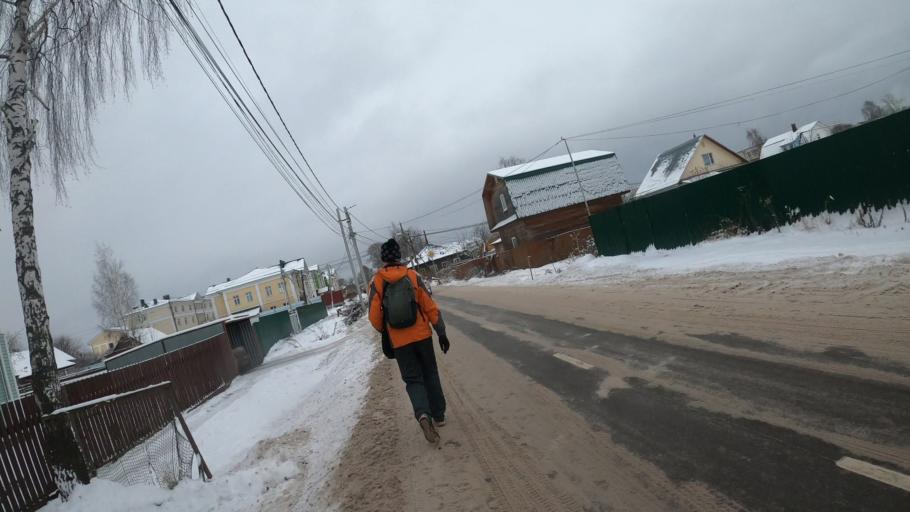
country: RU
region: Jaroslavl
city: Pereslavl'-Zalesskiy
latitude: 56.7264
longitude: 38.8361
